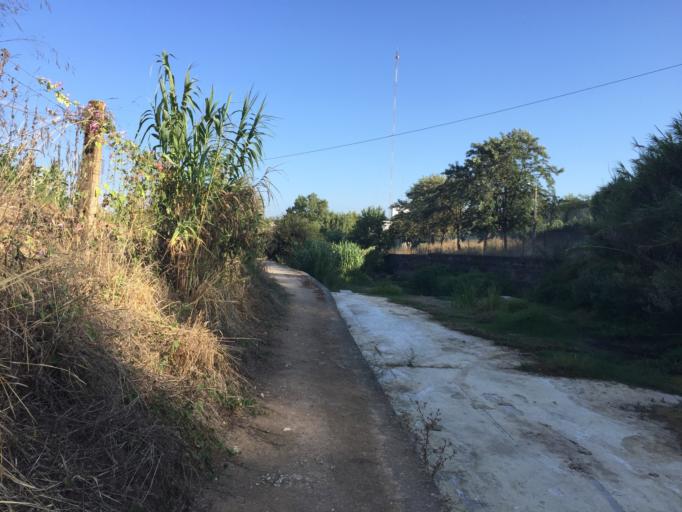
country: PT
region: Lisbon
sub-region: Alenquer
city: Alenquer
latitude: 39.1129
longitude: -8.9951
